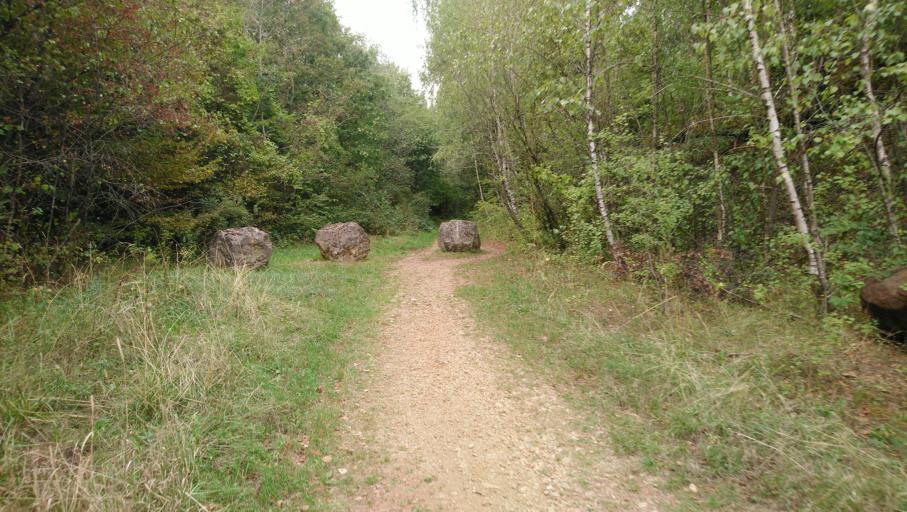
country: LU
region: Luxembourg
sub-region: Canton d'Esch-sur-Alzette
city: Obercorn
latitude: 49.5026
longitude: 5.9067
